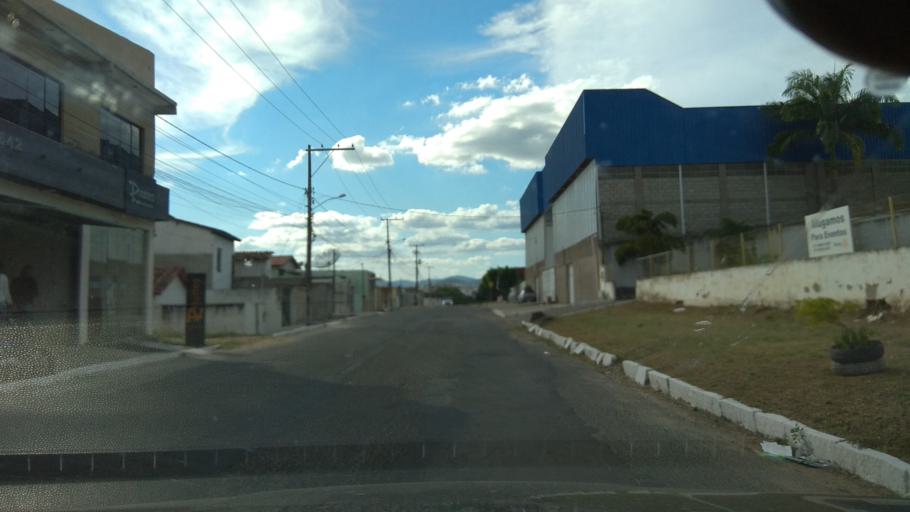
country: BR
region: Bahia
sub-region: Jequie
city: Jequie
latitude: -13.8748
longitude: -40.0744
